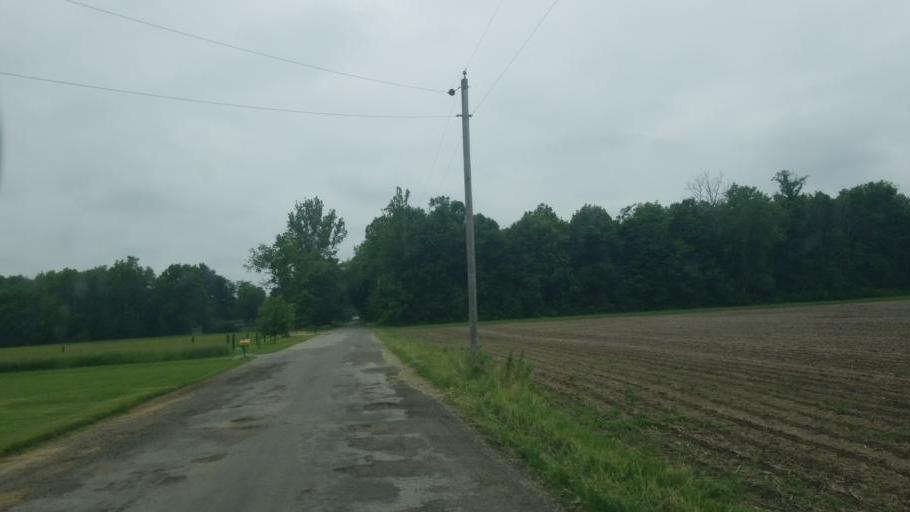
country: US
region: Indiana
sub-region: Elkhart County
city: Wakarusa
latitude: 41.4839
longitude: -86.0595
